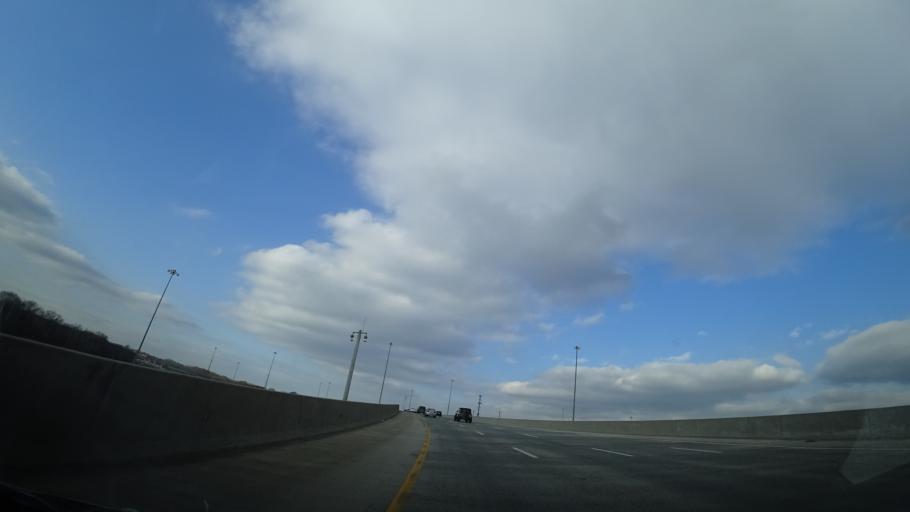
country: US
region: Virginia
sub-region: Fairfax County
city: Springfield
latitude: 38.7891
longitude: -77.1761
